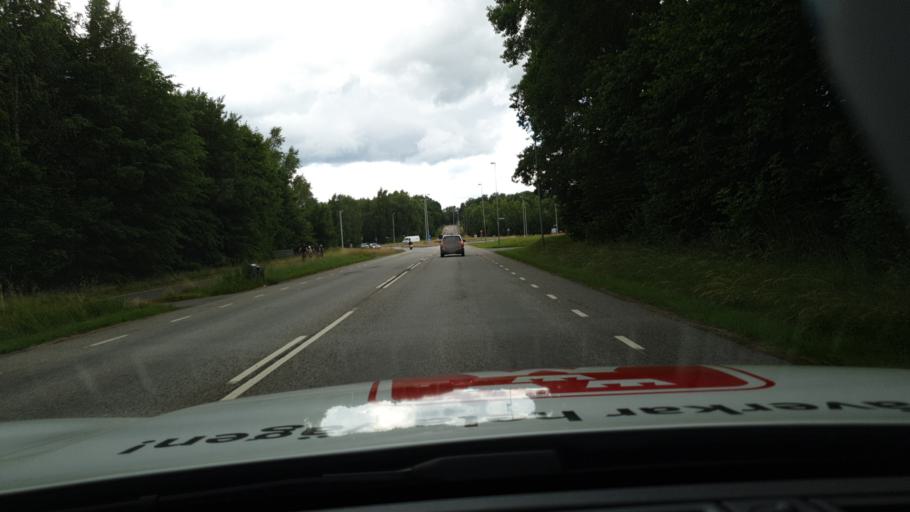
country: SE
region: Skane
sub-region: Hassleholms Kommun
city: Tormestorp
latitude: 56.1360
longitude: 13.7389
